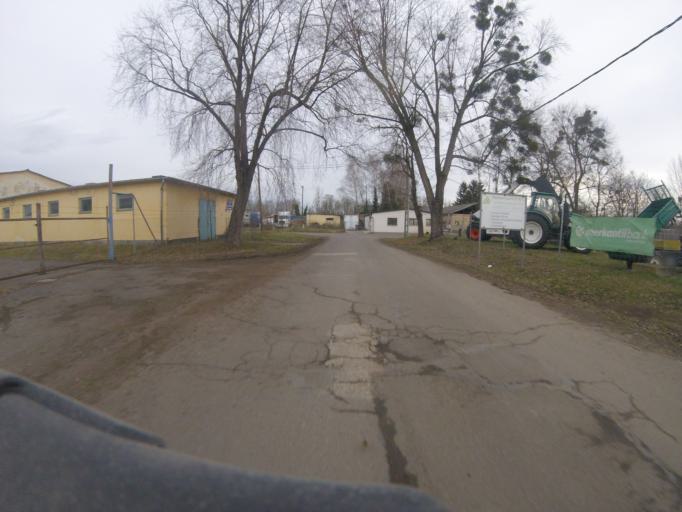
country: HU
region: Tolna
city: Dombovar
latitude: 46.3510
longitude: 18.1220
